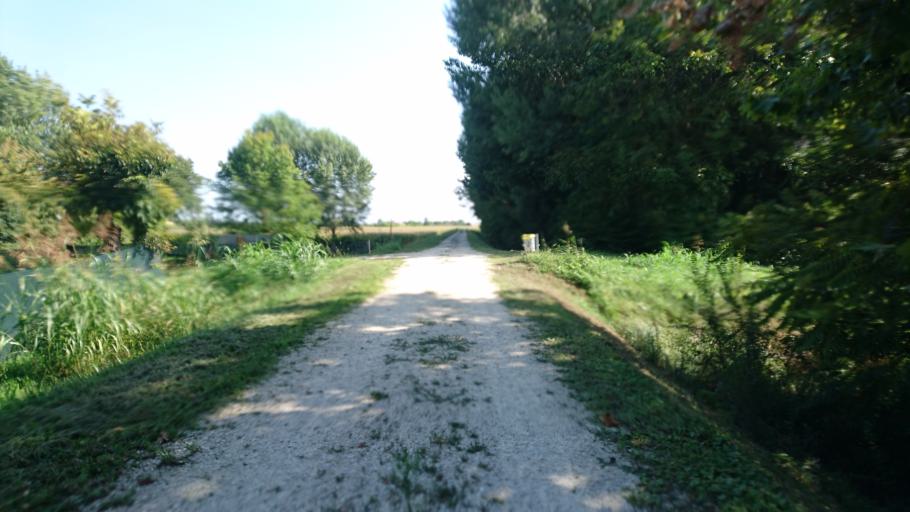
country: IT
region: Veneto
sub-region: Provincia di Padova
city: Veggiano
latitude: 45.4406
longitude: 11.7253
